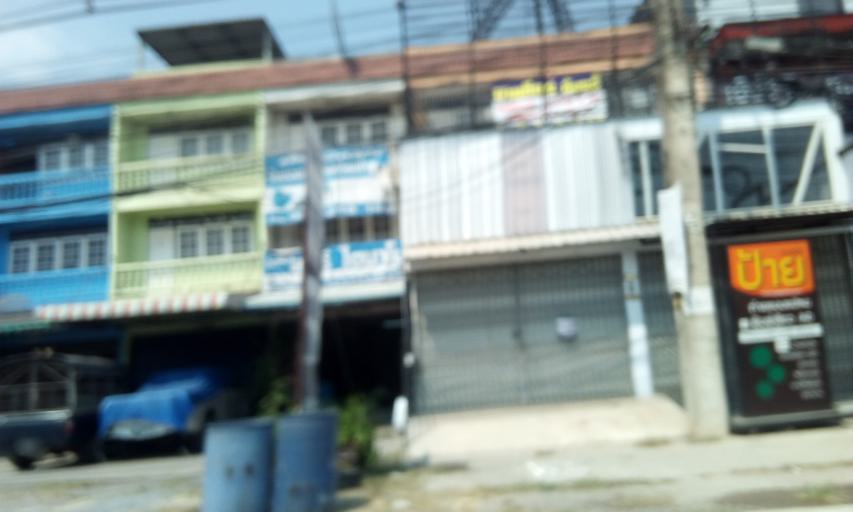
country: TH
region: Nakhon Nayok
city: Ongkharak
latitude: 14.0850
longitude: 100.9160
